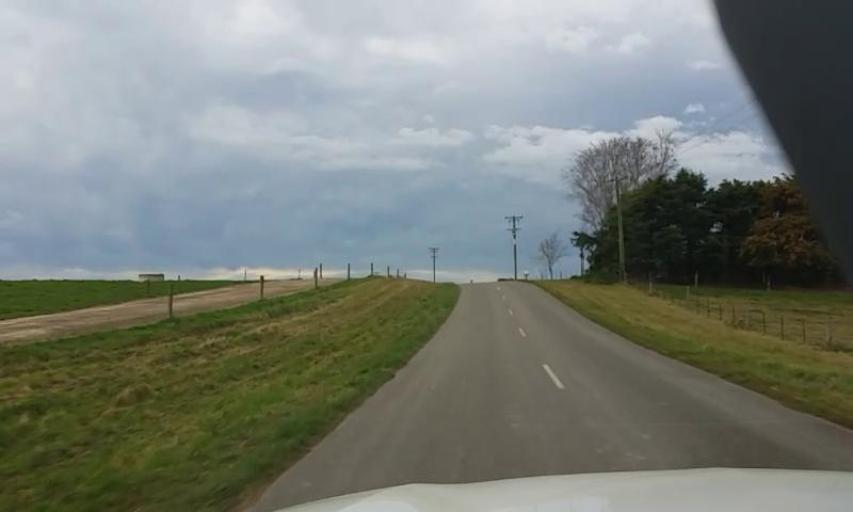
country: NZ
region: Canterbury
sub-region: Waimakariri District
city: Kaiapoi
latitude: -43.2961
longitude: 172.4759
